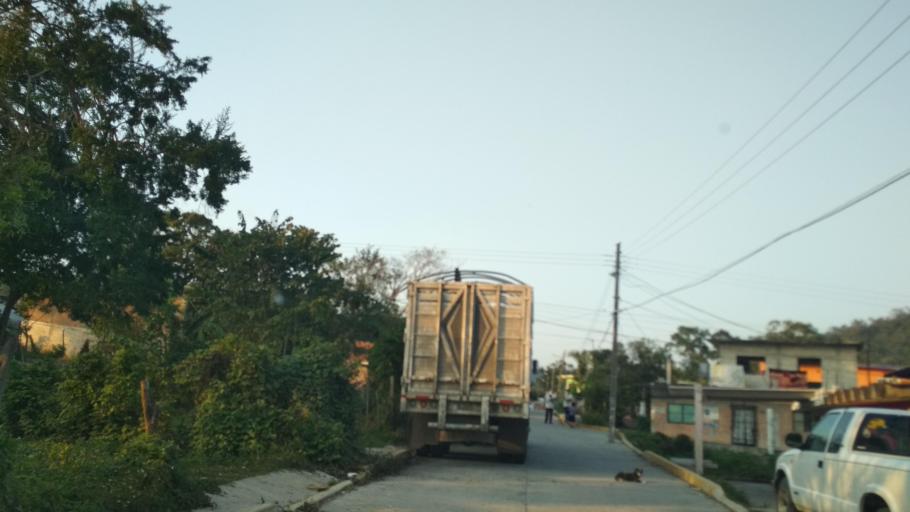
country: MM
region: Shan
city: Taunggyi
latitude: 20.4076
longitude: 97.3369
